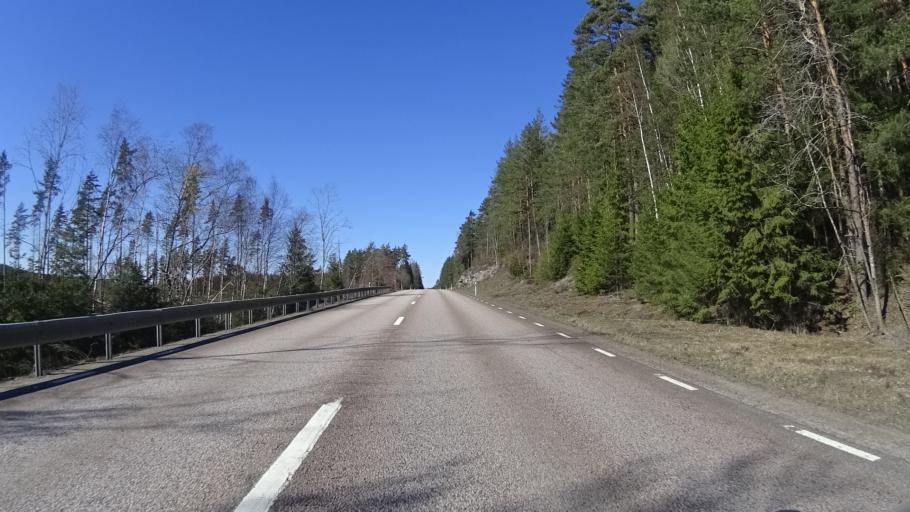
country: SE
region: Vaermland
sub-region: Karlstads Kommun
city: Edsvalla
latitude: 59.5840
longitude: 13.0146
